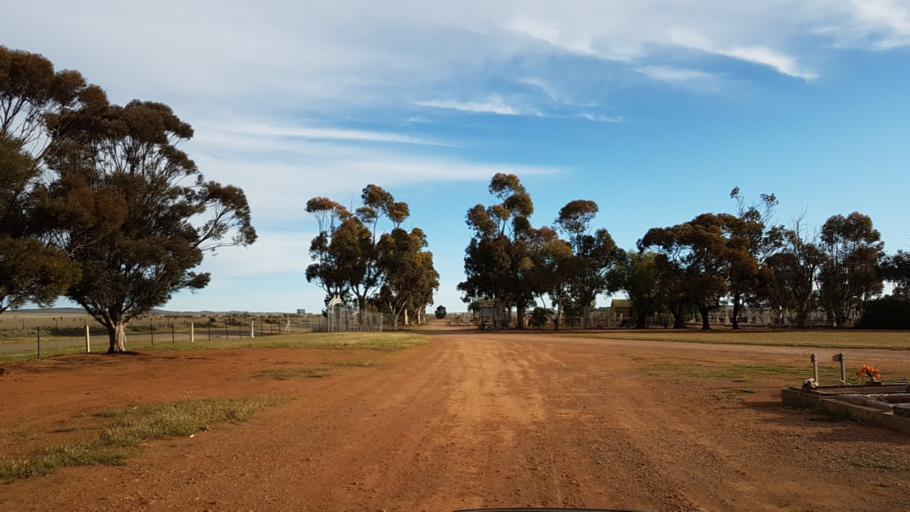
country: AU
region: South Australia
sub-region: Peterborough
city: Peterborough
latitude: -32.9825
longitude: 138.8512
